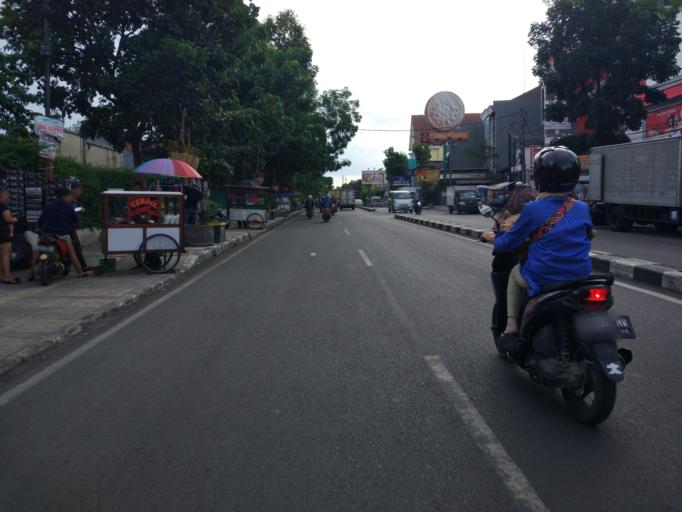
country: ID
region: West Java
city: Bandung
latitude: -6.9183
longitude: 107.5828
